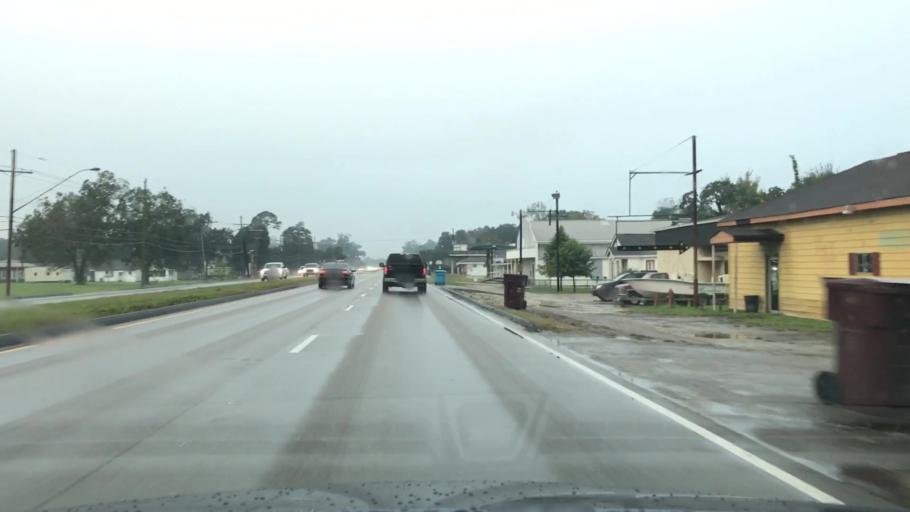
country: US
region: Louisiana
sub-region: Saint Charles Parish
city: Paradis
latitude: 29.8801
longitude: -90.4313
